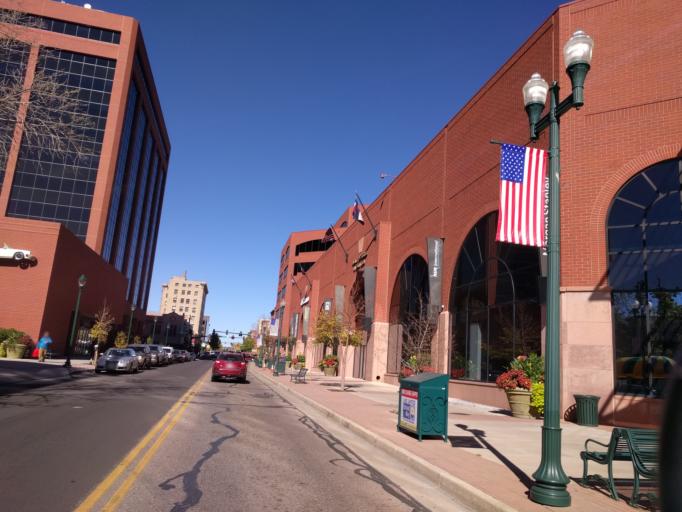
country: US
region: Colorado
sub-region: El Paso County
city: Colorado Springs
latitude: 38.8313
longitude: -104.8237
